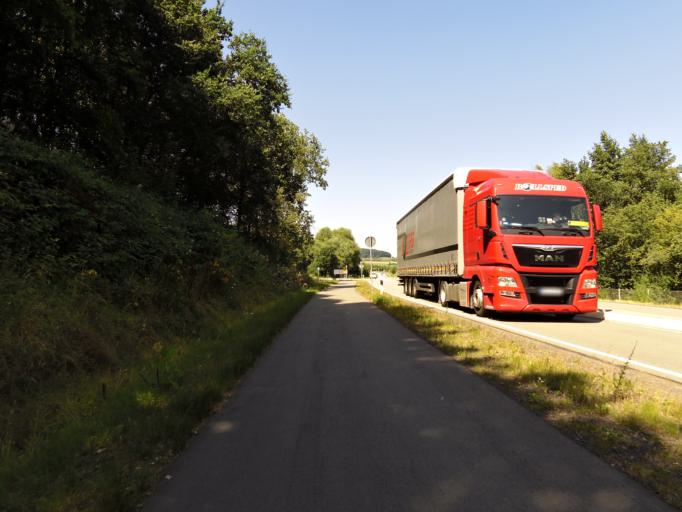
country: DE
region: Rheinland-Pfalz
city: Munchweiler an der Alsenz
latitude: 49.5276
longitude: 7.8880
